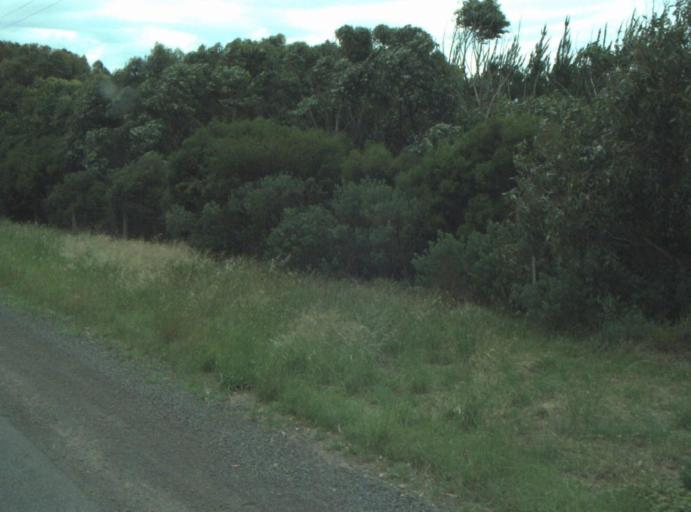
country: AU
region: Victoria
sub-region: Greater Geelong
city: Leopold
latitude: -38.1984
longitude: 144.4671
